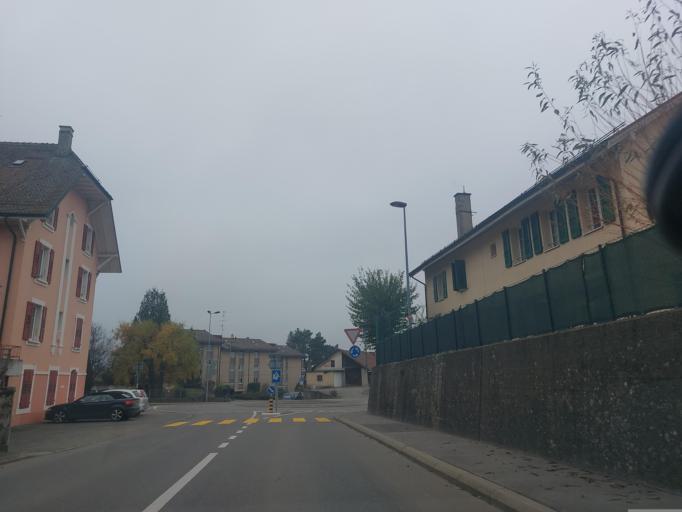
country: CH
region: Vaud
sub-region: Lavaux-Oron District
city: Palezieux
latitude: 46.5441
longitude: 6.8405
